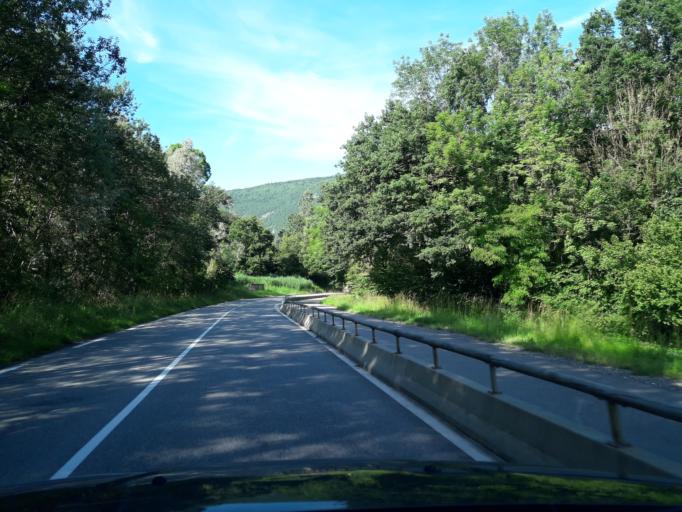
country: FR
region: Rhone-Alpes
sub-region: Departement de la Savoie
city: Novalaise
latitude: 45.5598
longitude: 5.7907
